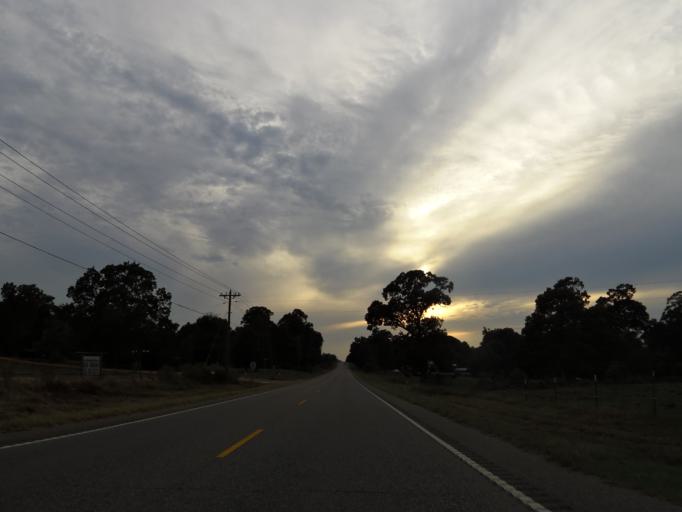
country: US
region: Alabama
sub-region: Escambia County
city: Atmore
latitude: 31.0060
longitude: -87.5779
